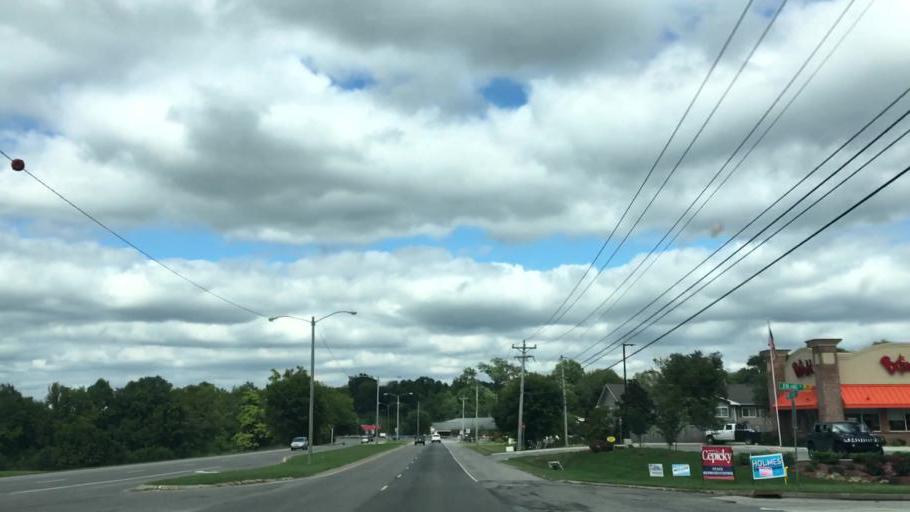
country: US
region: Tennessee
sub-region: Maury County
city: Columbia
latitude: 35.6136
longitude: -87.0669
